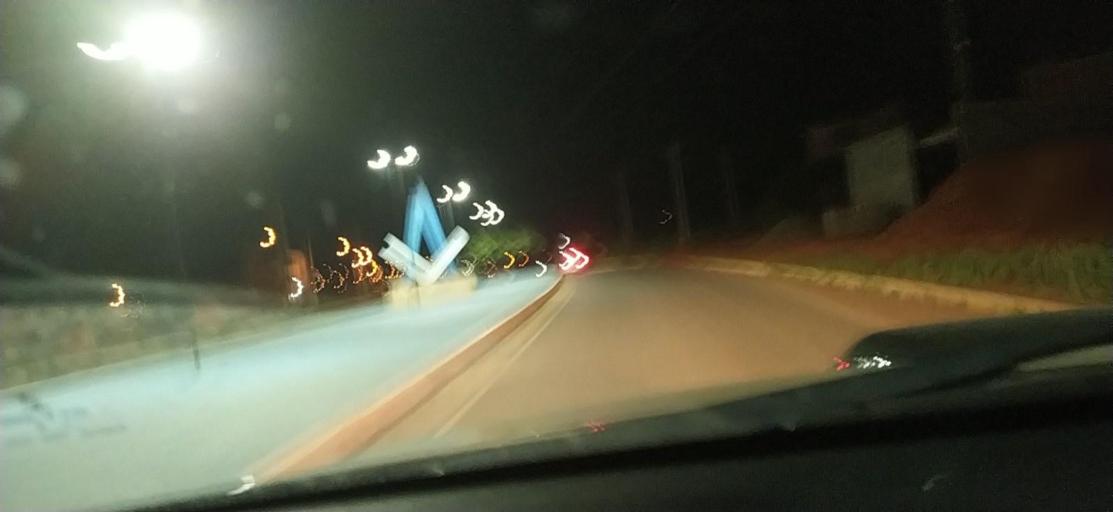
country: BR
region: Minas Gerais
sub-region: Monte Azul
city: Monte Azul
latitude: -15.1605
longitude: -42.8677
